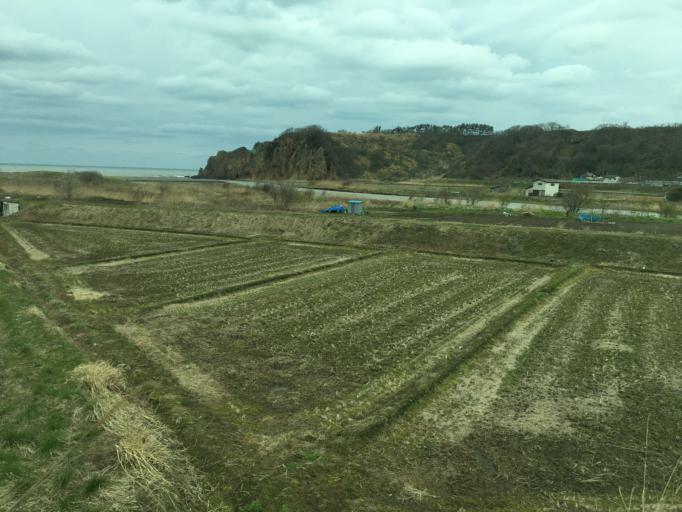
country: JP
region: Aomori
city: Shimokizukuri
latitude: 40.6830
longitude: 139.9689
